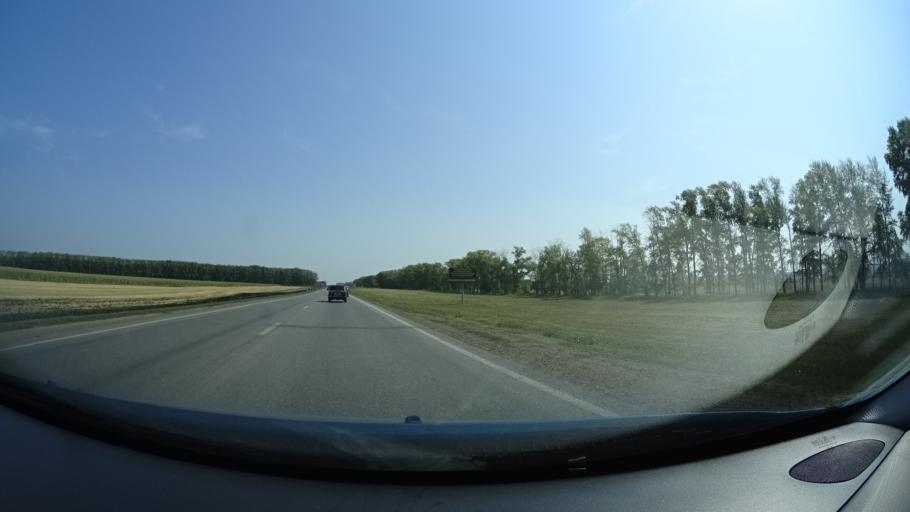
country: RU
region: Bashkortostan
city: Karmaskaly
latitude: 54.3852
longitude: 56.1675
